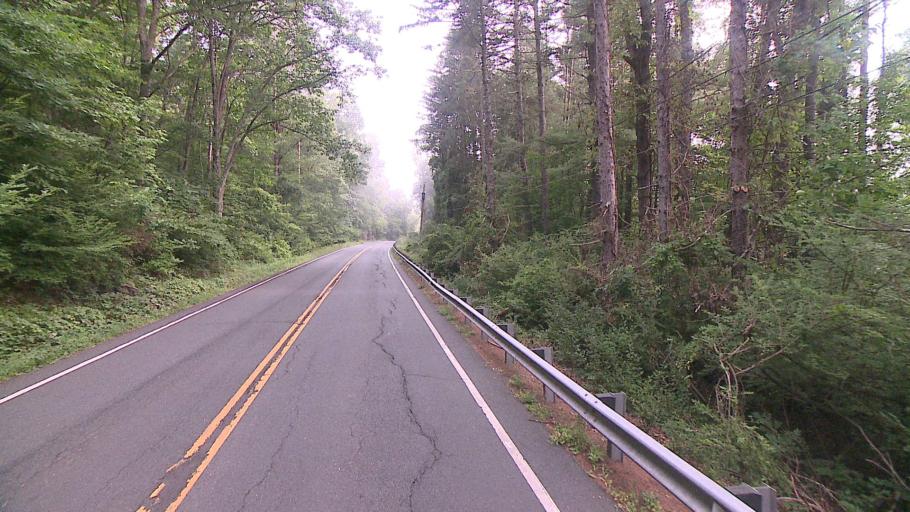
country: US
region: Connecticut
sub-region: Litchfield County
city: Canaan
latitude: 41.9209
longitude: -73.3647
